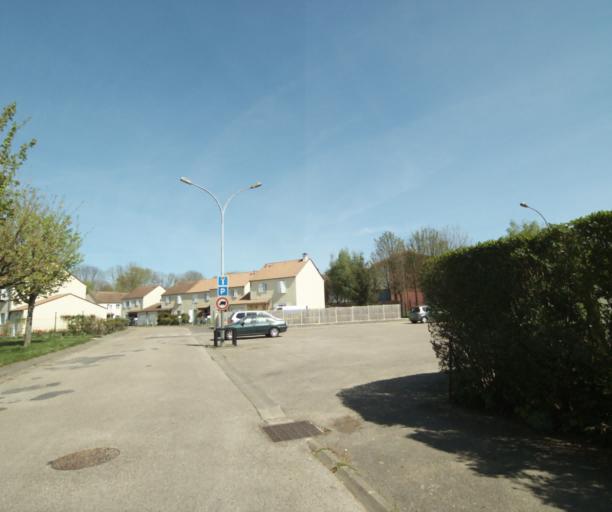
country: FR
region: Ile-de-France
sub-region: Departement de Seine-et-Marne
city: Nangis
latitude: 48.5522
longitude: 3.0110
